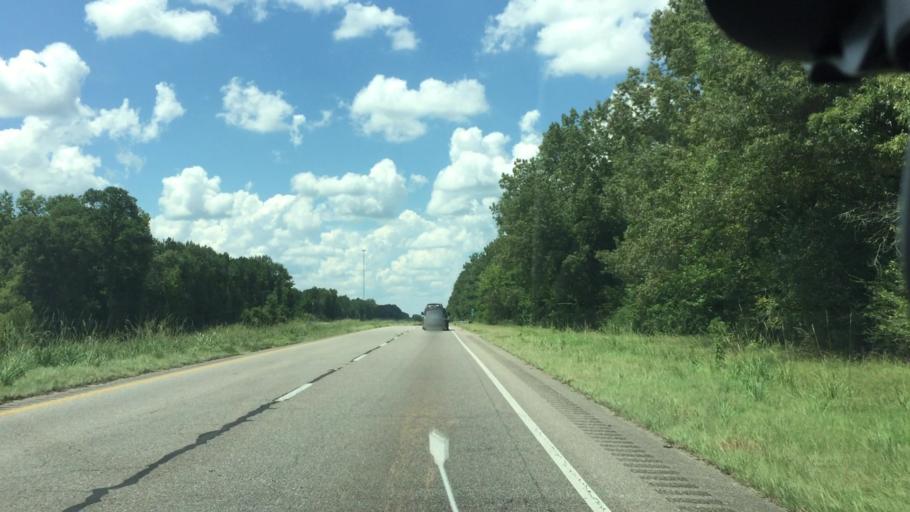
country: US
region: Alabama
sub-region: Montgomery County
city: Pike Road
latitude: 32.1209
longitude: -86.0726
